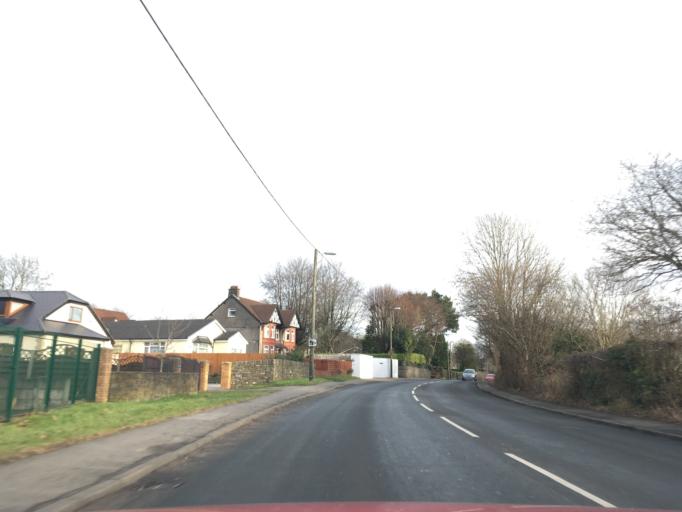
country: GB
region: Wales
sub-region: Caerphilly County Borough
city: Bedwas
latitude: 51.5918
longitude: -3.1784
